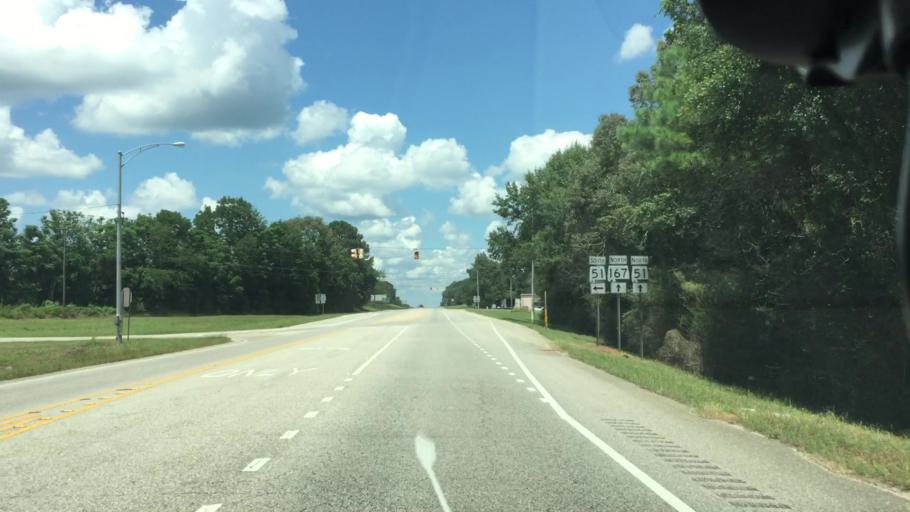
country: US
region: Alabama
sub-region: Coffee County
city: New Brockton
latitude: 31.4252
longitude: -85.8879
